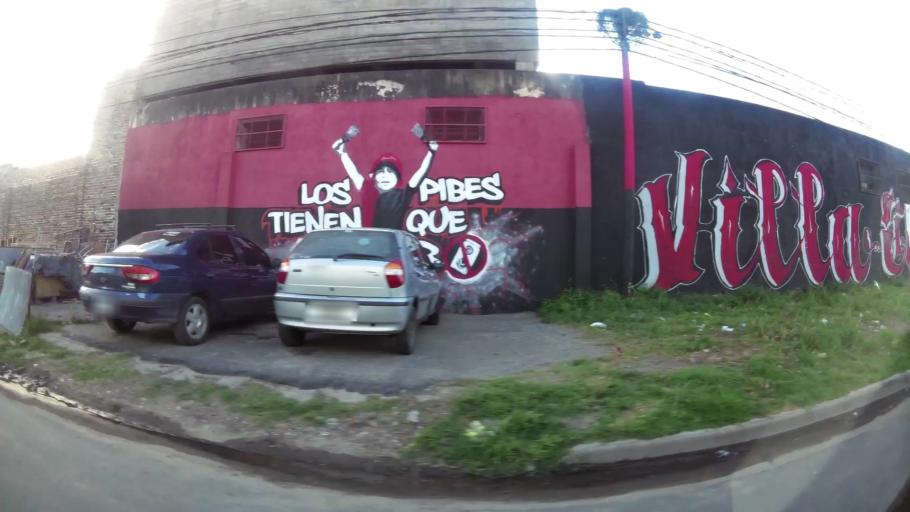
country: AR
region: Santa Fe
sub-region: Departamento de Rosario
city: Rosario
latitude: -32.9793
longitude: -60.6696
